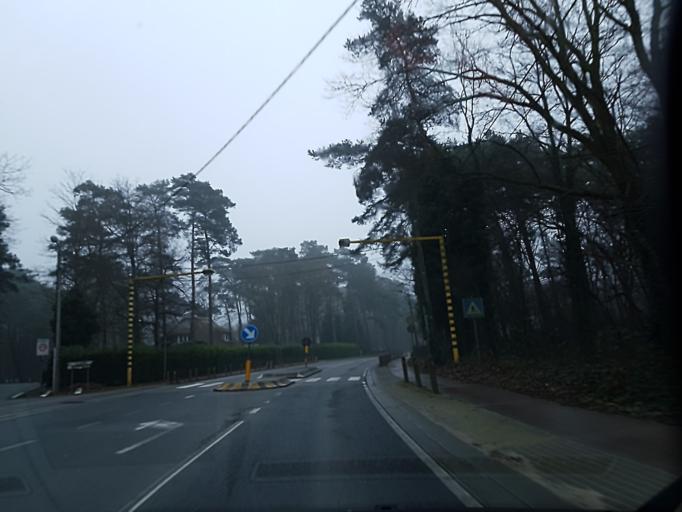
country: BE
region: Flanders
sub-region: Provincie Antwerpen
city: Bonheiden
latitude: 51.0175
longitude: 4.5757
